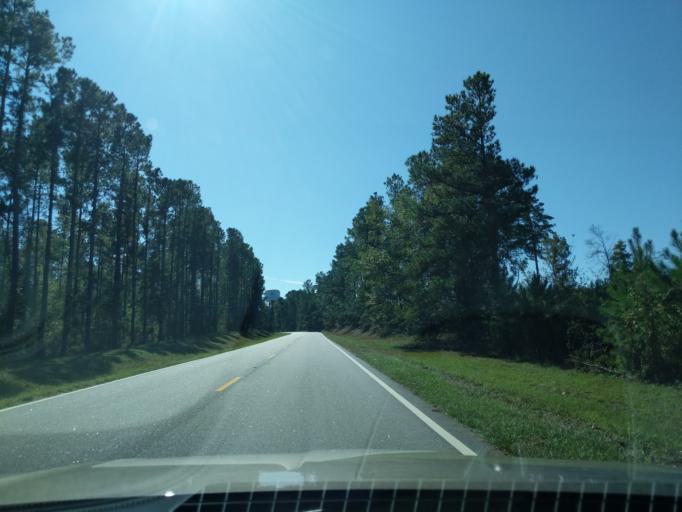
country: US
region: Georgia
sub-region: Richmond County
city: Hephzibah
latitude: 33.2773
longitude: -82.0153
